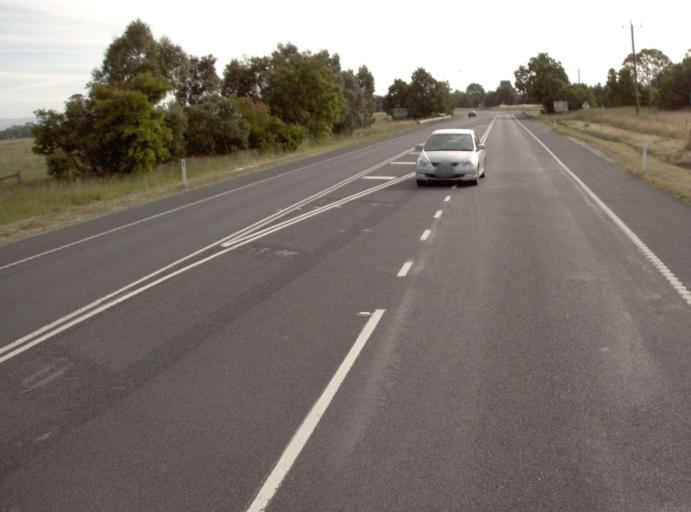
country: AU
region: Victoria
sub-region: Latrobe
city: Traralgon
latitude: -38.1295
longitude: 146.5626
